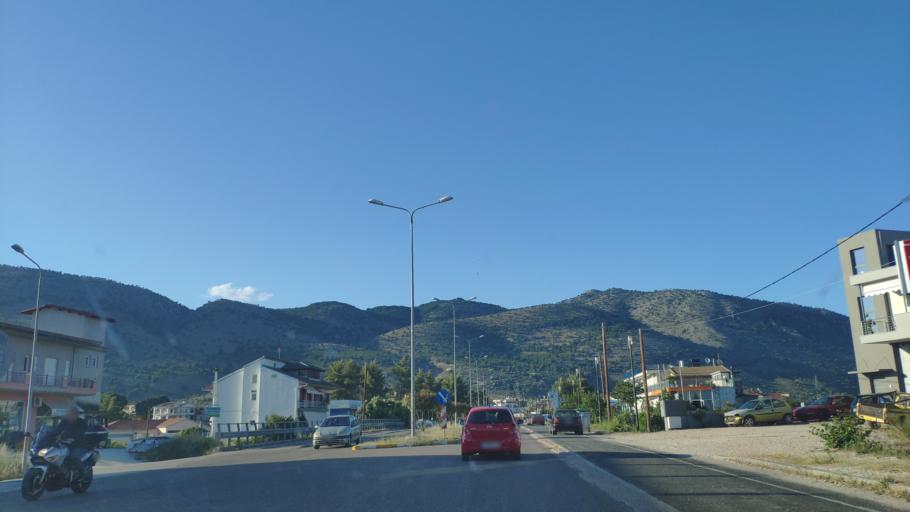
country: GR
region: Epirus
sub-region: Nomos Prevezis
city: Louros
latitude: 39.1621
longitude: 20.7544
